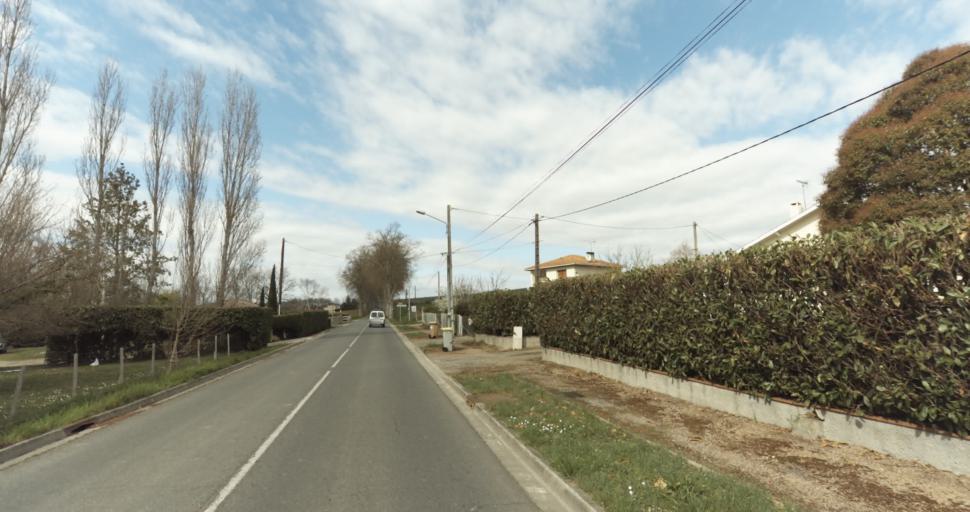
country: FR
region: Midi-Pyrenees
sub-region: Departement de la Haute-Garonne
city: Auterive
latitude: 43.3598
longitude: 1.4765
